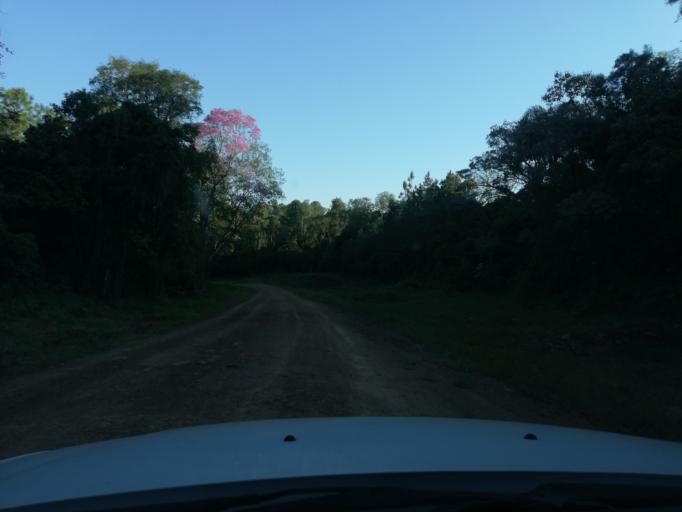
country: AR
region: Misiones
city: Cerro Cora
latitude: -27.6184
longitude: -55.7063
